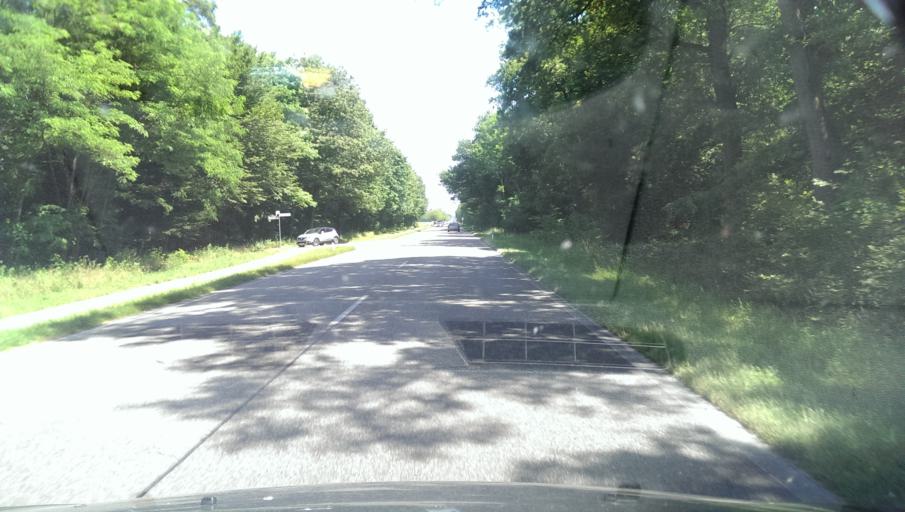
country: DE
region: Baden-Wuerttemberg
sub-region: Karlsruhe Region
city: Muggensturm
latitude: 48.8947
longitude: 8.2928
